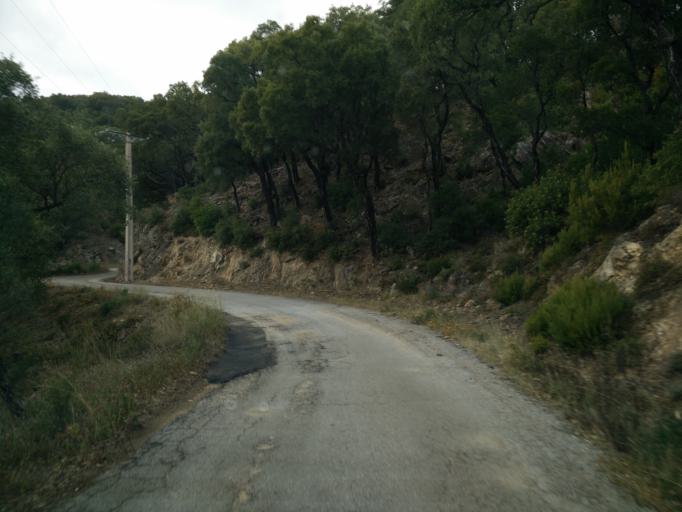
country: FR
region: Provence-Alpes-Cote d'Azur
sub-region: Departement du Var
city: Roquebrune-sur-Argens
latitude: 43.3851
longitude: 6.6125
